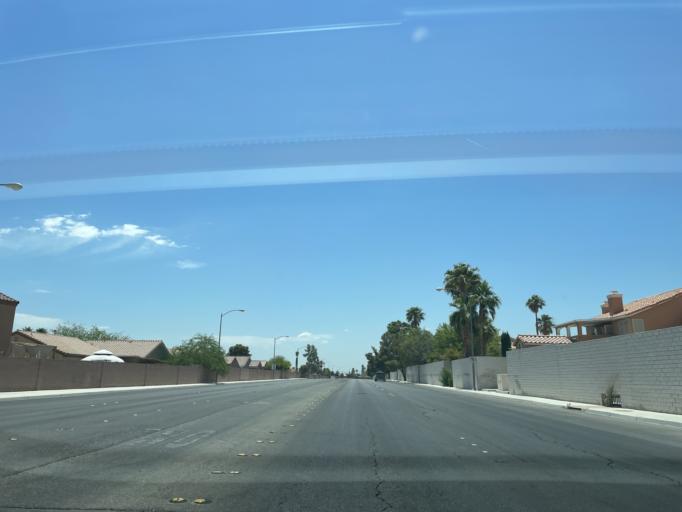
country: US
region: Nevada
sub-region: Clark County
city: North Las Vegas
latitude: 36.2690
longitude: -115.1532
